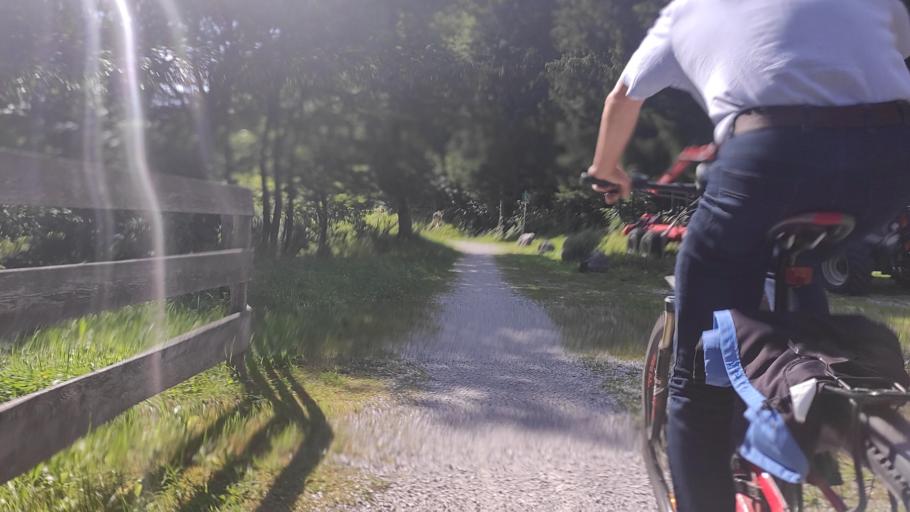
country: AT
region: Salzburg
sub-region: Politischer Bezirk Zell am See
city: Lofer
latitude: 47.5799
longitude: 12.6784
